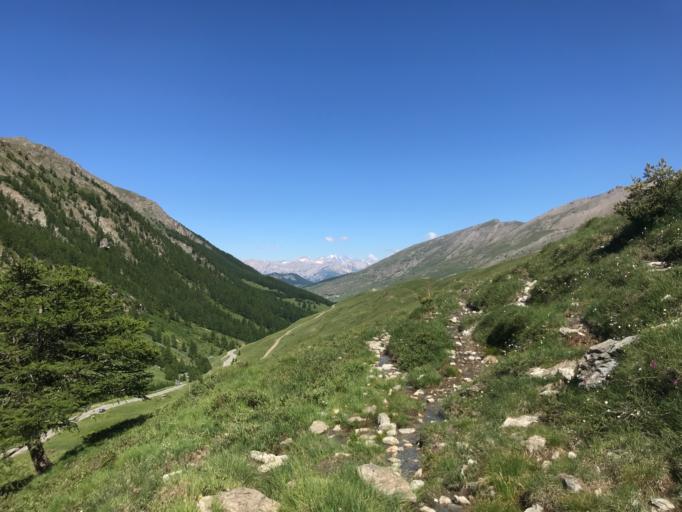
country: IT
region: Piedmont
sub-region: Provincia di Cuneo
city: Pontechianale
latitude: 44.7056
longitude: 6.9343
